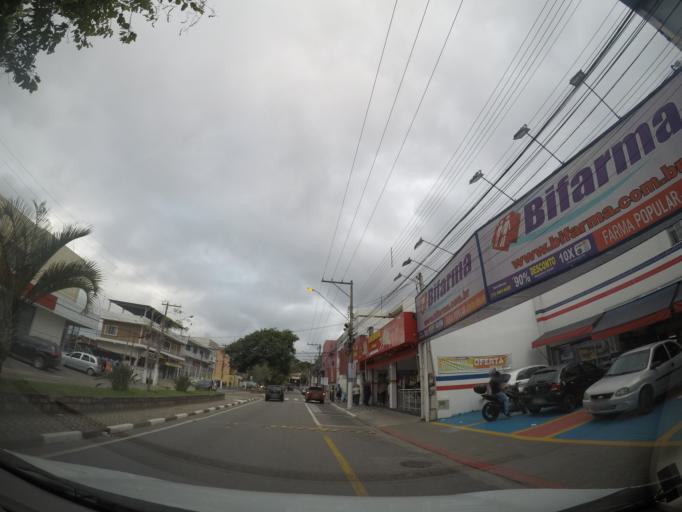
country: BR
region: Sao Paulo
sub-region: Aruja
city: Aruja
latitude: -23.3942
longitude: -46.3240
